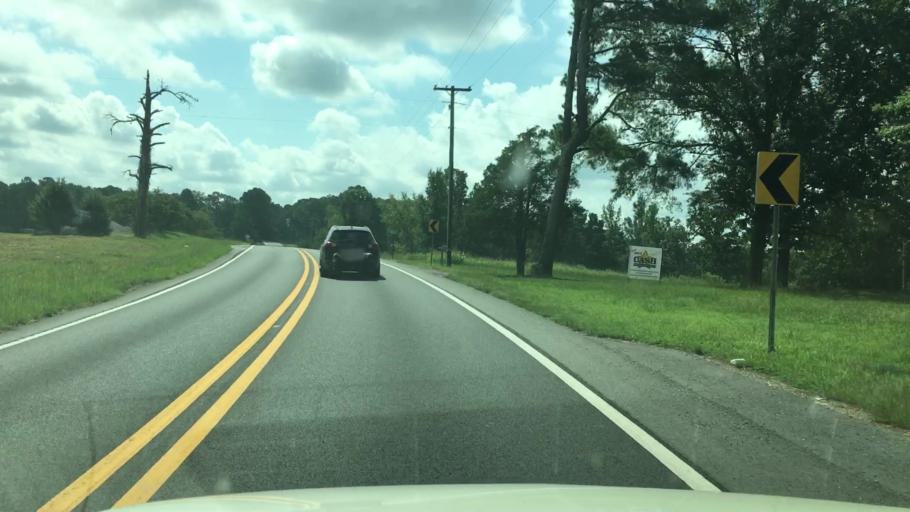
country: US
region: Arkansas
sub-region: Garland County
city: Lake Hamilton
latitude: 34.2818
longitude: -93.1622
